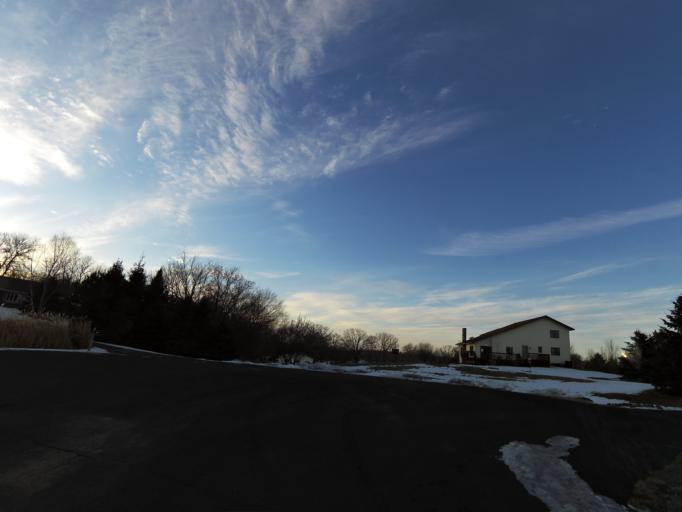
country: US
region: Minnesota
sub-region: Washington County
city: Lake Elmo
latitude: 44.9793
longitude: -92.8613
